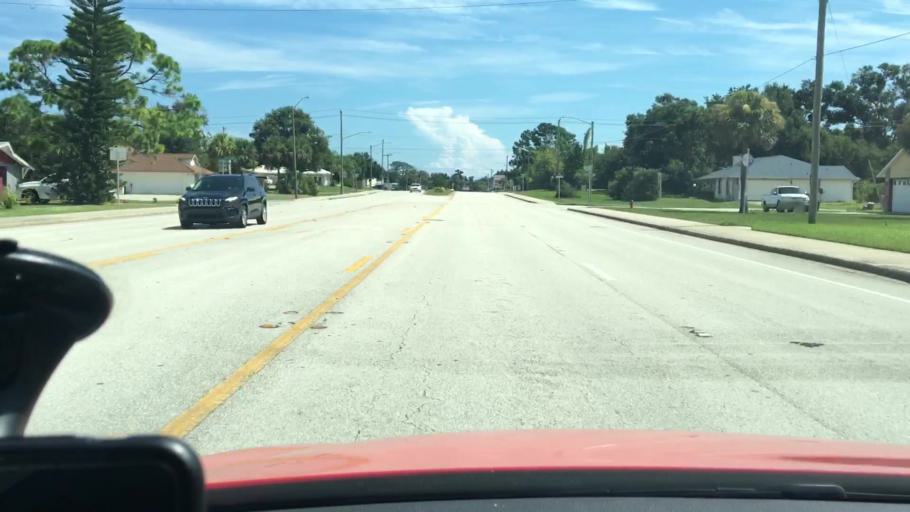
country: US
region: Florida
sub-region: Volusia County
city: Edgewater
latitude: 28.9706
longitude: -80.9005
